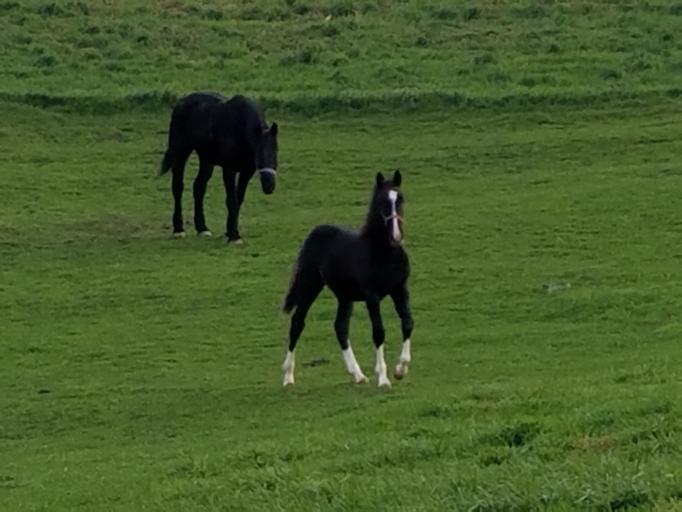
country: US
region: Wisconsin
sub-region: Vernon County
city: Hillsboro
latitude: 43.6067
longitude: -90.4269
